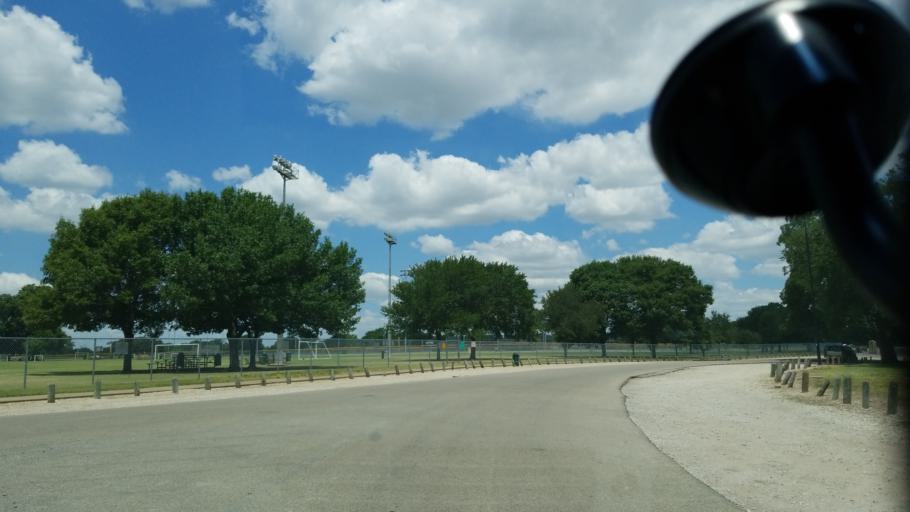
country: US
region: Texas
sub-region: Dallas County
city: Cockrell Hill
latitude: 32.7098
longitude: -96.8503
